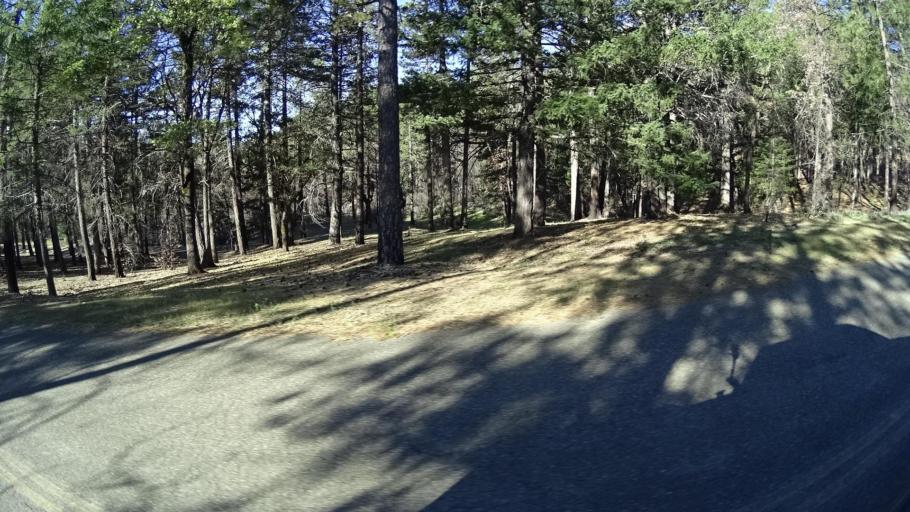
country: US
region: California
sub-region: Lake County
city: Upper Lake
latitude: 39.3074
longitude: -122.9368
